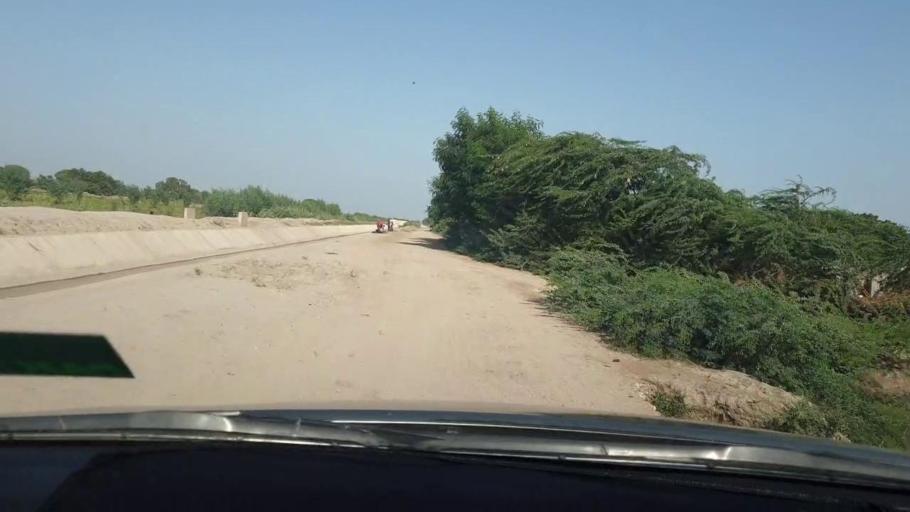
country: PK
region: Sindh
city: Naukot
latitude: 24.9272
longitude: 69.2491
